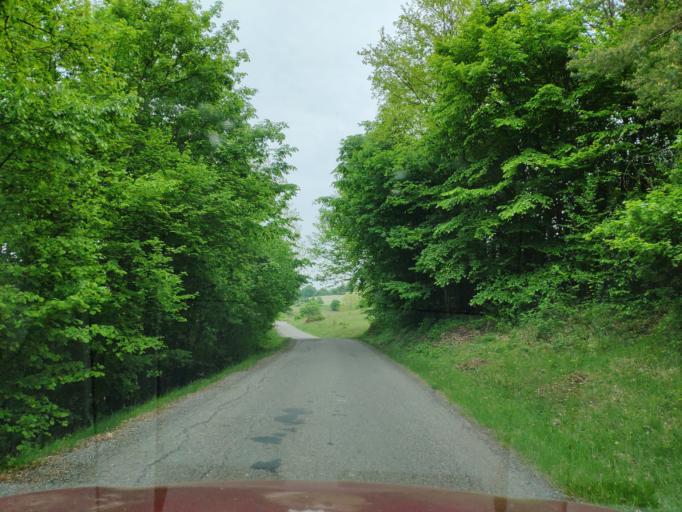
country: SK
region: Banskobystricky
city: Revuca
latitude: 48.5275
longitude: 20.1140
